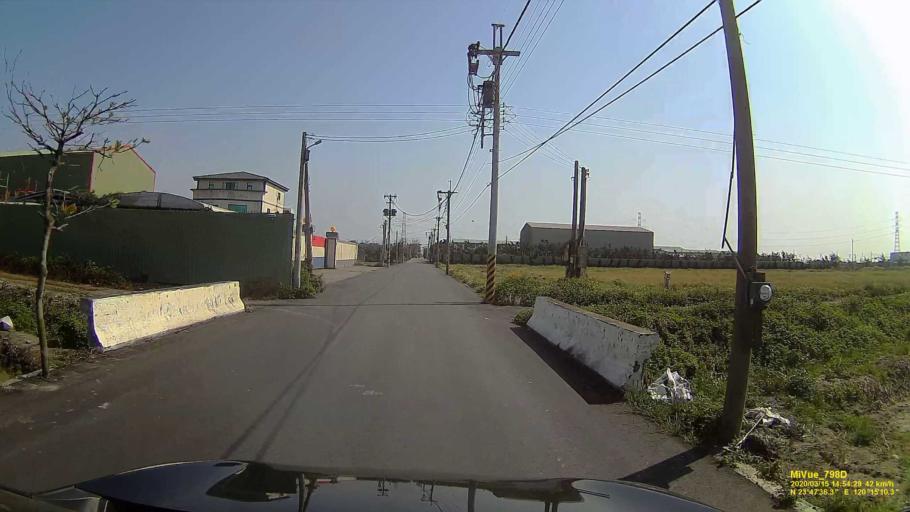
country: TW
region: Taiwan
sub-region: Yunlin
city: Douliu
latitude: 23.7931
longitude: 120.2529
